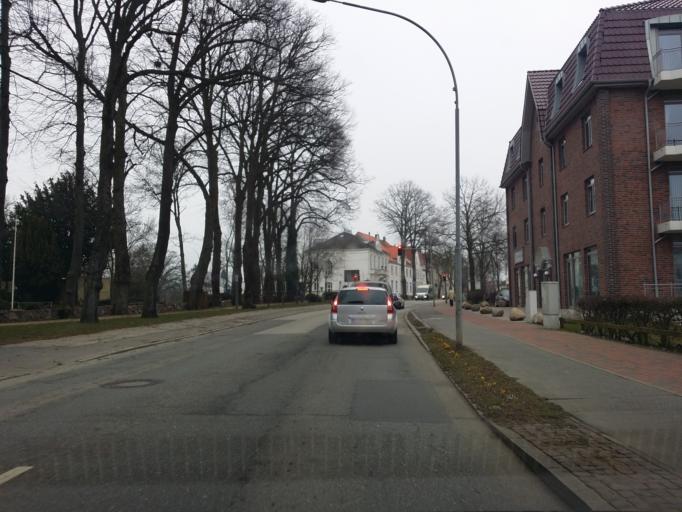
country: DE
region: Schleswig-Holstein
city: Fehmarn
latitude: 54.4411
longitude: 11.1918
